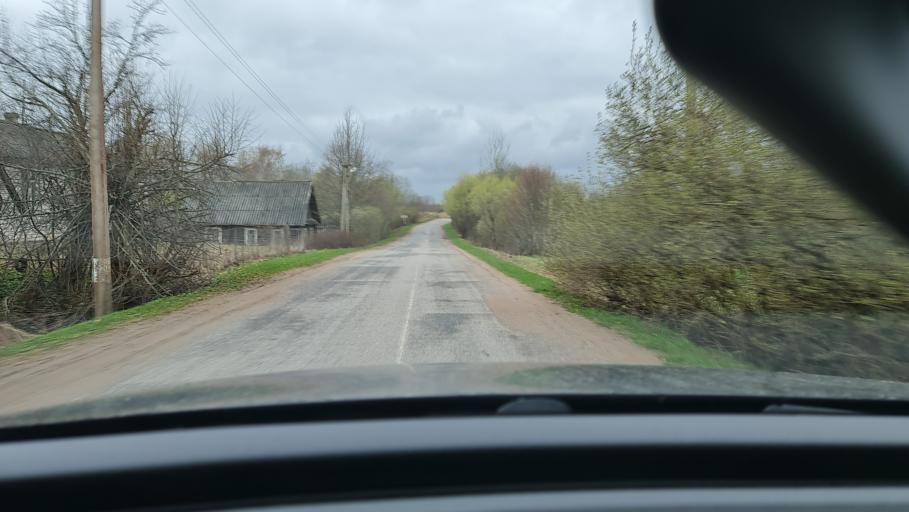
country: RU
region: Novgorod
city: Marevo
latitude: 57.1087
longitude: 31.7820
